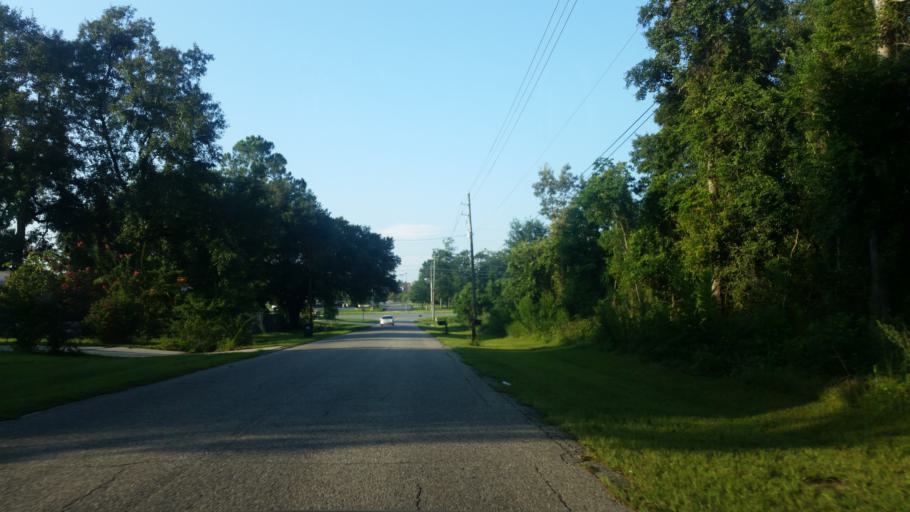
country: US
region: Florida
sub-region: Escambia County
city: Ferry Pass
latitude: 30.5339
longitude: -87.2267
